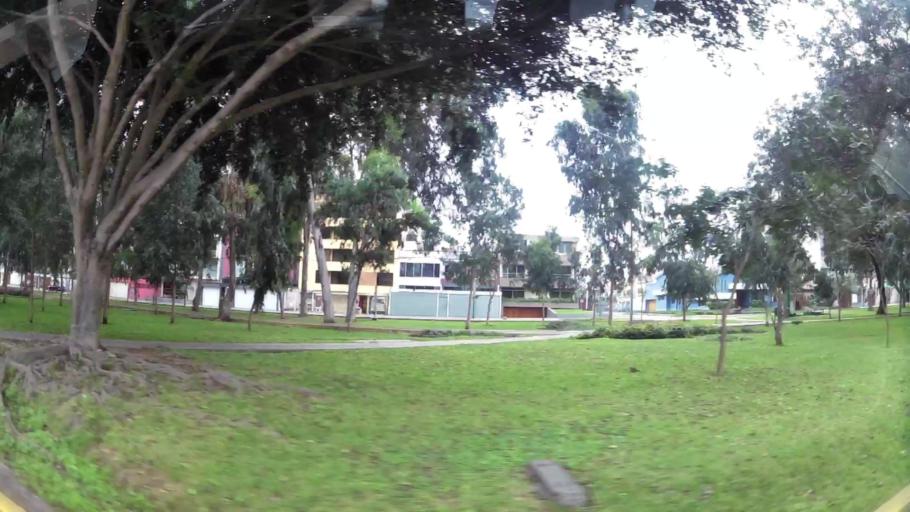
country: PE
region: Lima
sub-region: Lima
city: San Luis
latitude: -12.1014
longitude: -77.0044
